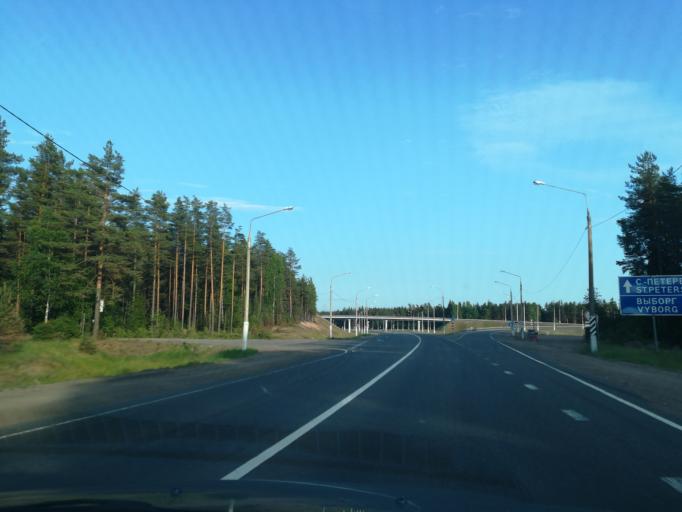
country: RU
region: Leningrad
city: Vyborg
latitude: 60.6767
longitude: 28.8692
